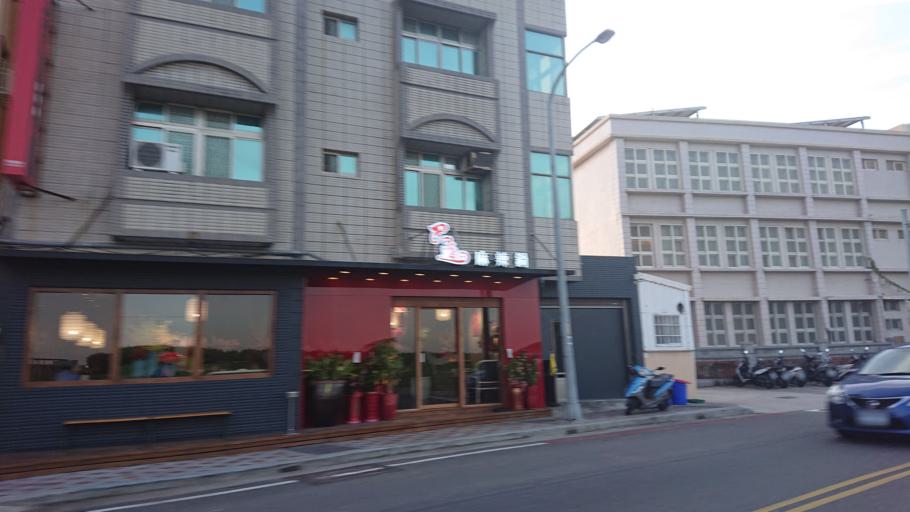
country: TW
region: Taiwan
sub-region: Penghu
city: Ma-kung
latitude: 23.5719
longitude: 119.5816
